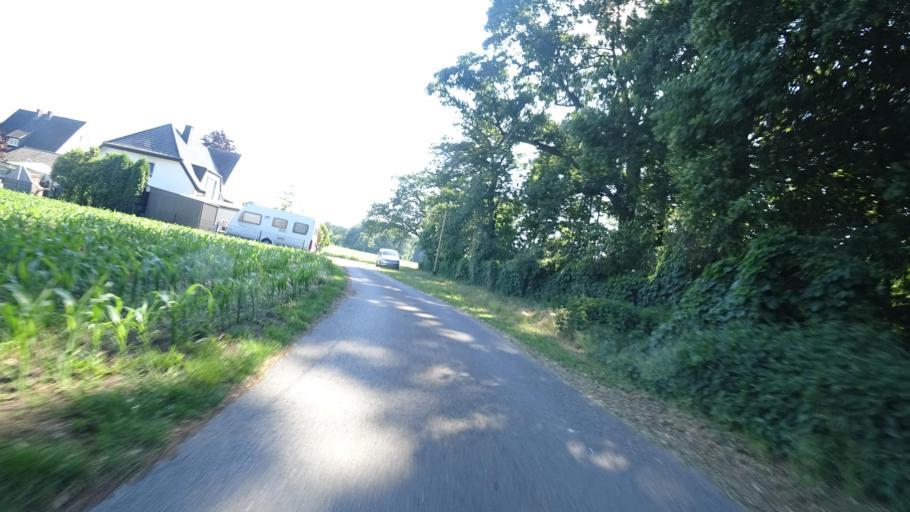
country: DE
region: North Rhine-Westphalia
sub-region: Regierungsbezirk Detmold
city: Guetersloh
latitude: 51.8982
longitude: 8.3369
